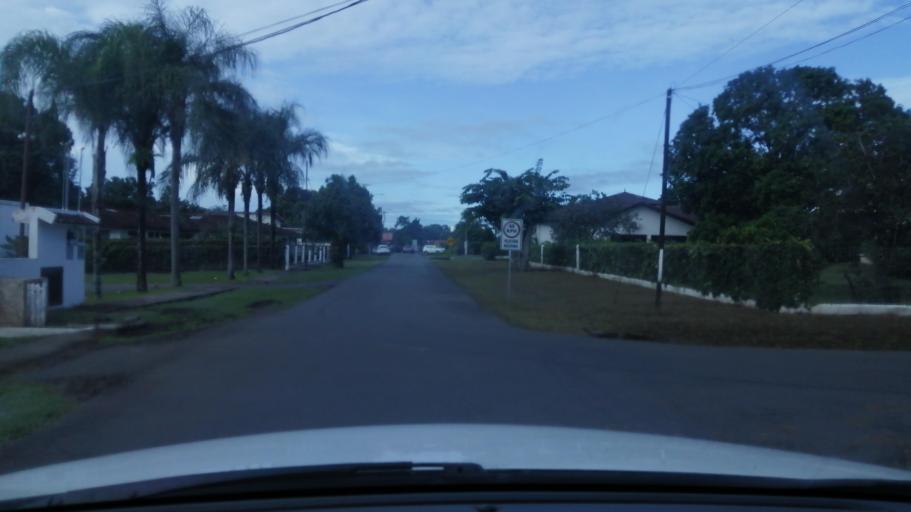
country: PA
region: Chiriqui
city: Mata del Nance
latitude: 8.4545
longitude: -82.4185
